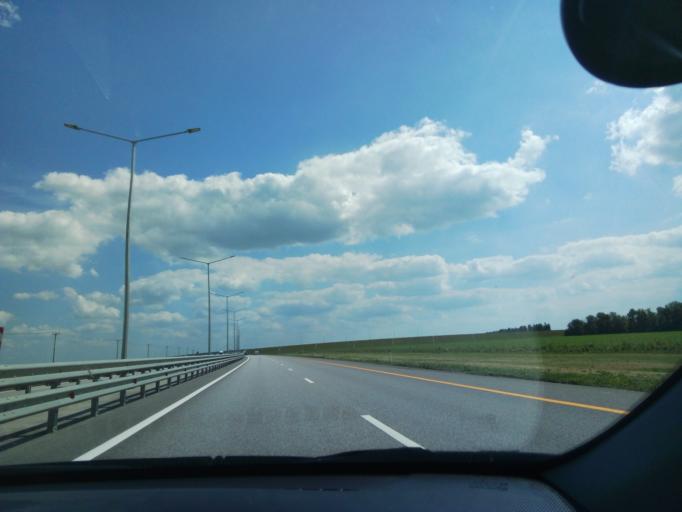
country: RU
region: Voronezj
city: Podkletnoye
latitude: 51.5115
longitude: 39.5132
